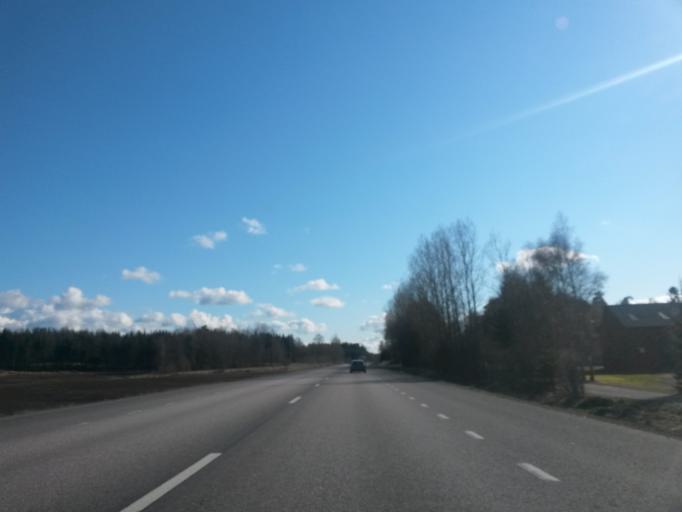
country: SE
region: Vaestra Goetaland
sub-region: Vargarda Kommun
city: Vargarda
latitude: 58.1319
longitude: 12.8583
